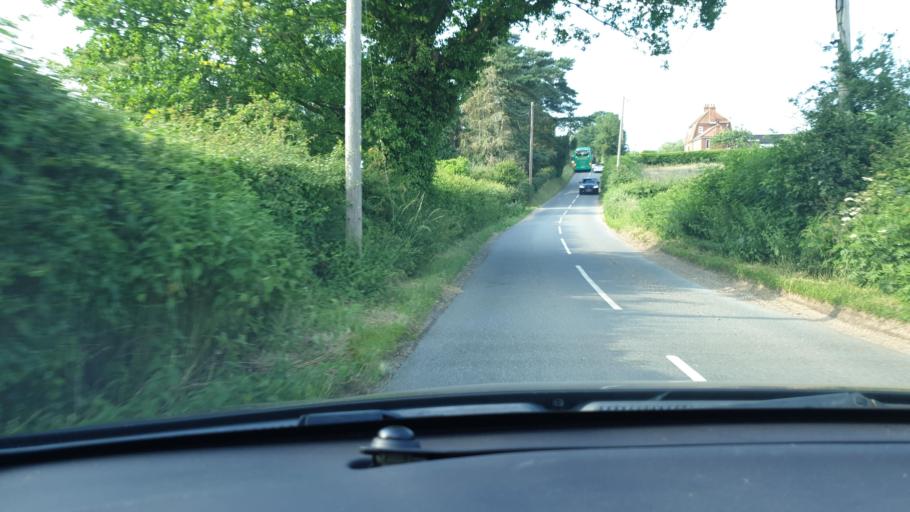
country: GB
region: England
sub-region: Essex
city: Little Clacton
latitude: 51.8626
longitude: 1.1200
